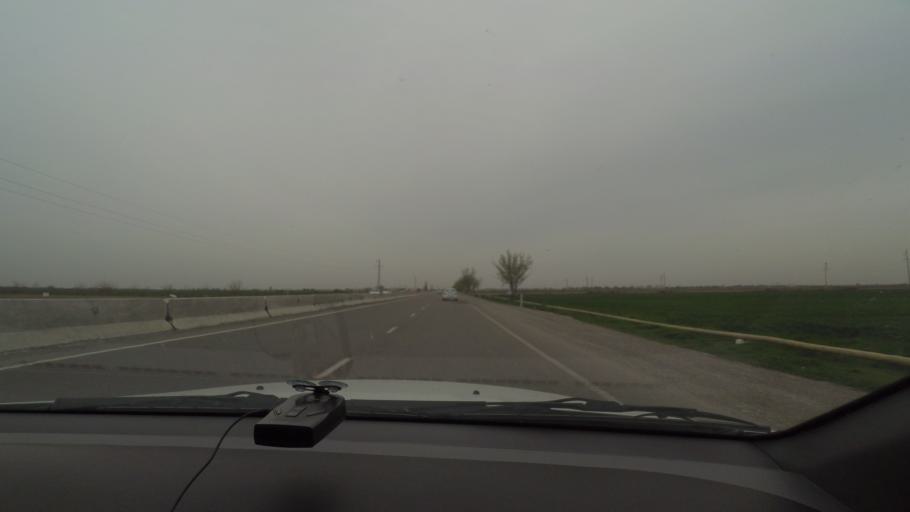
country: KZ
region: Ongtustik Qazaqstan
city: Myrzakent
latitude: 40.5586
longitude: 68.3869
